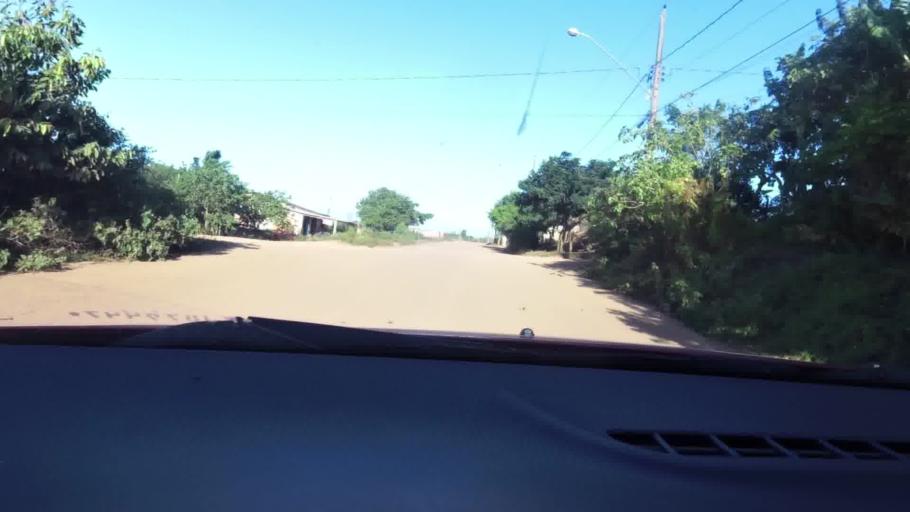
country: BR
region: Espirito Santo
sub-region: Guarapari
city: Guarapari
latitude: -20.5537
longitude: -40.4133
